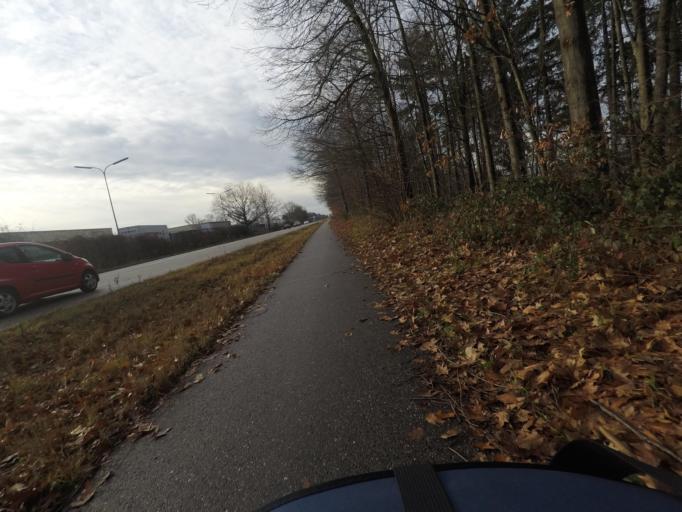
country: DE
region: Baden-Wuerttemberg
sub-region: Karlsruhe Region
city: Muggensturm
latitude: 48.8871
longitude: 8.2738
